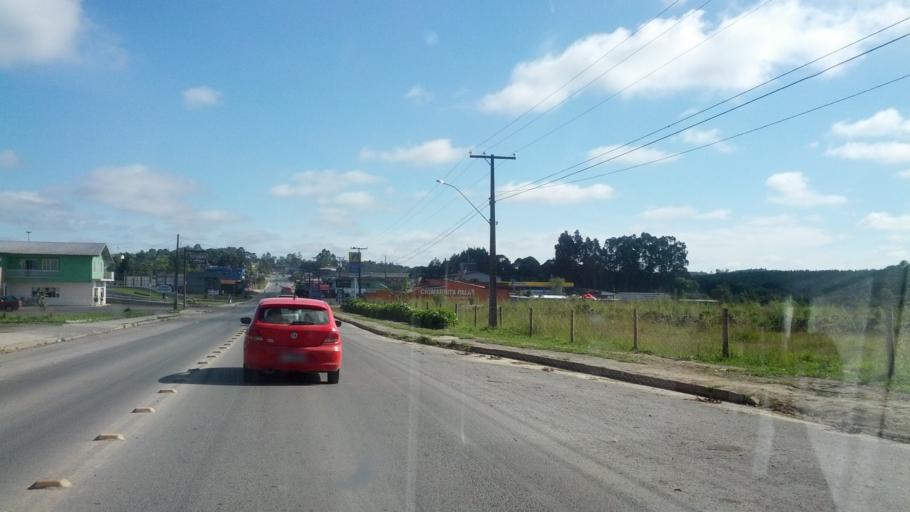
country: BR
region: Santa Catarina
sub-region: Otacilio Costa
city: Otacilio Costa
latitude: -27.4957
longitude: -50.1214
